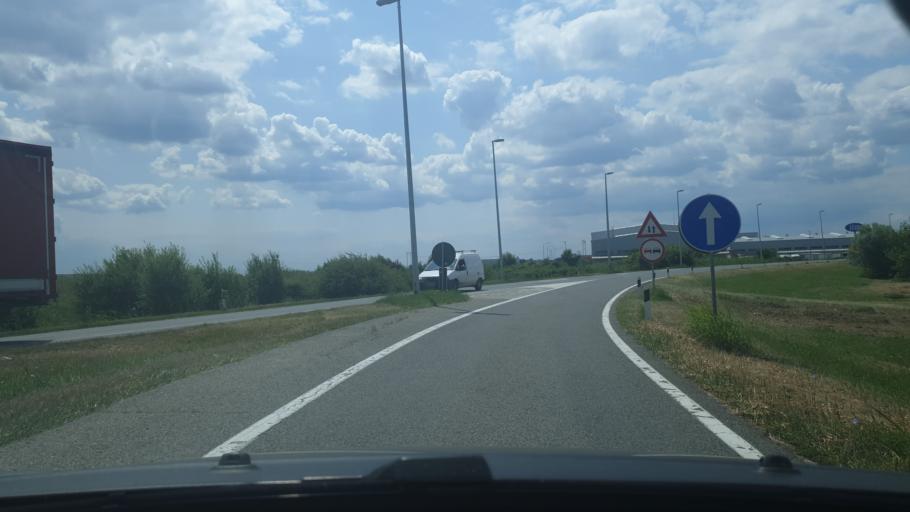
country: RS
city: Simanovci
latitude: 44.8755
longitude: 20.1247
